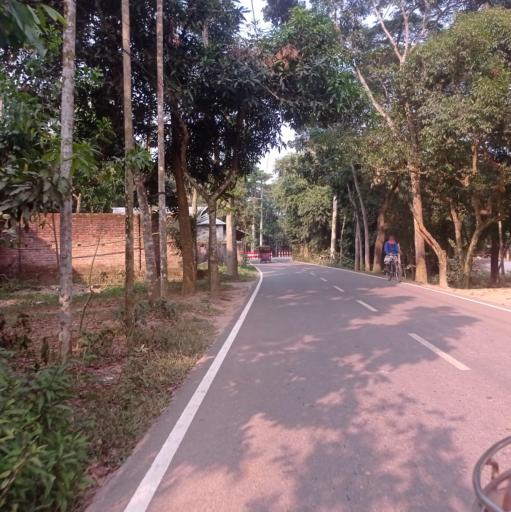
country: BD
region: Dhaka
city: Bhairab Bazar
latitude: 24.0781
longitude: 90.8479
